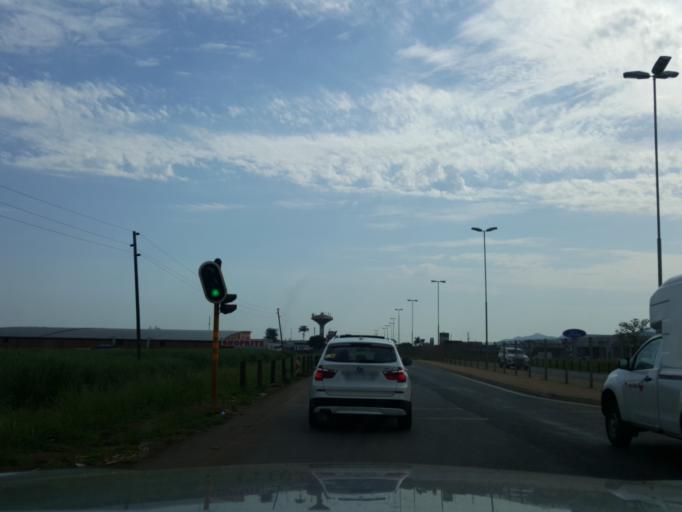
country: SZ
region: Hhohho
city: Ntfonjeni
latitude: -25.5018
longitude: 31.5040
